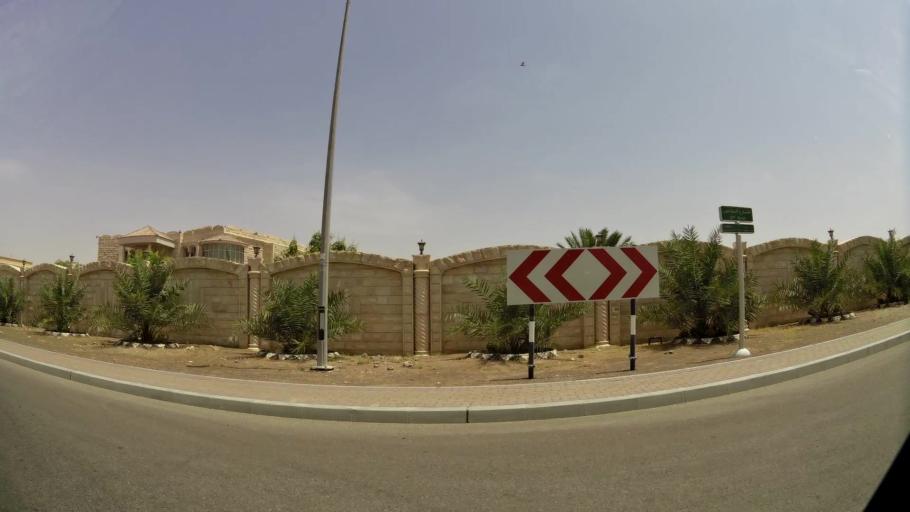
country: AE
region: Abu Dhabi
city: Al Ain
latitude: 24.2027
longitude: 55.7426
